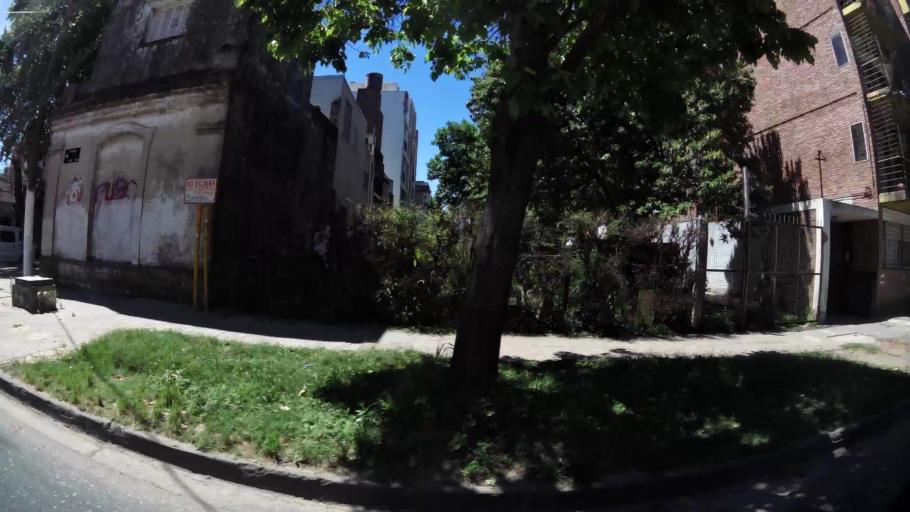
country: AR
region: Santa Fe
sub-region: Departamento de Rosario
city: Rosario
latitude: -32.9366
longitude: -60.6654
